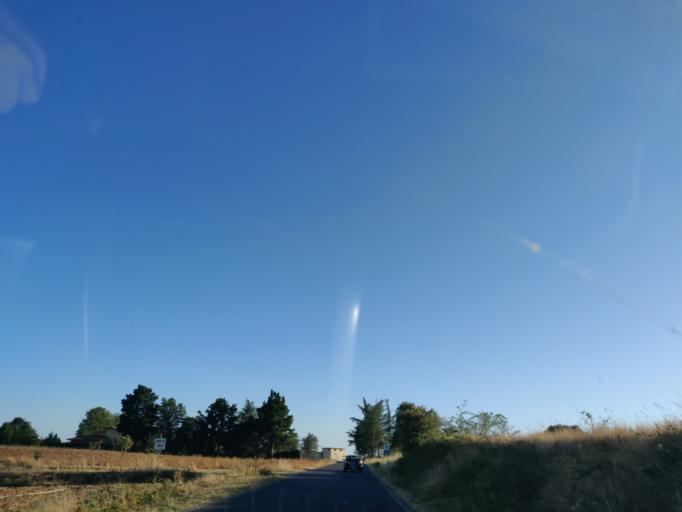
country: IT
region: Latium
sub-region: Provincia di Viterbo
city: Acquapendente
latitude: 42.7239
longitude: 11.8743
